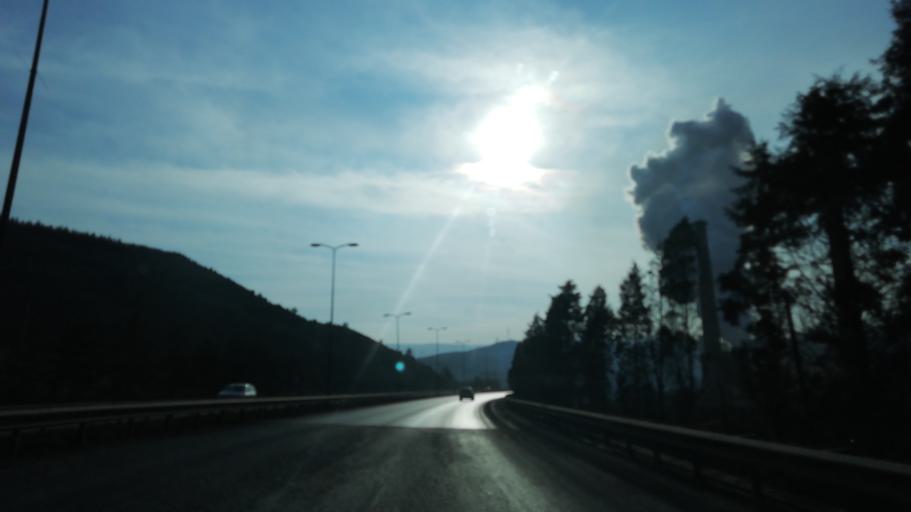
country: TR
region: Karabuk
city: Karabuk
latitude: 41.1778
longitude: 32.6382
